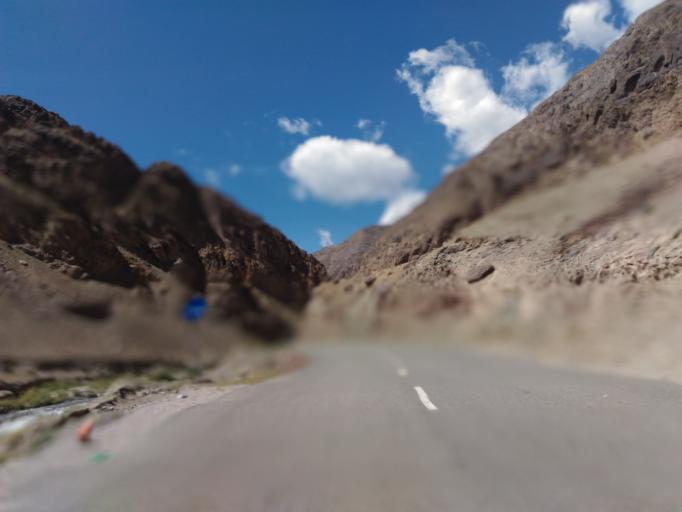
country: IN
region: Kashmir
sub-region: Ladakh
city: Leh
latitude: 33.8102
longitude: 77.8049
